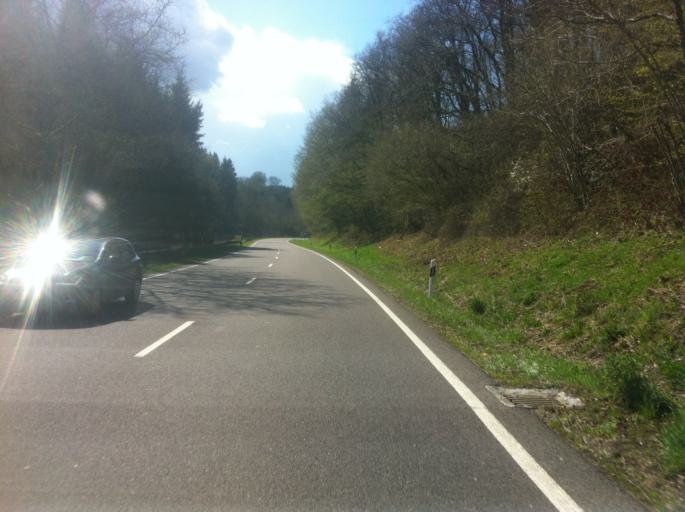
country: LU
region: Diekirch
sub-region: Canton de Wiltz
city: Esch-sur-Sure
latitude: 49.9331
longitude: 5.9248
